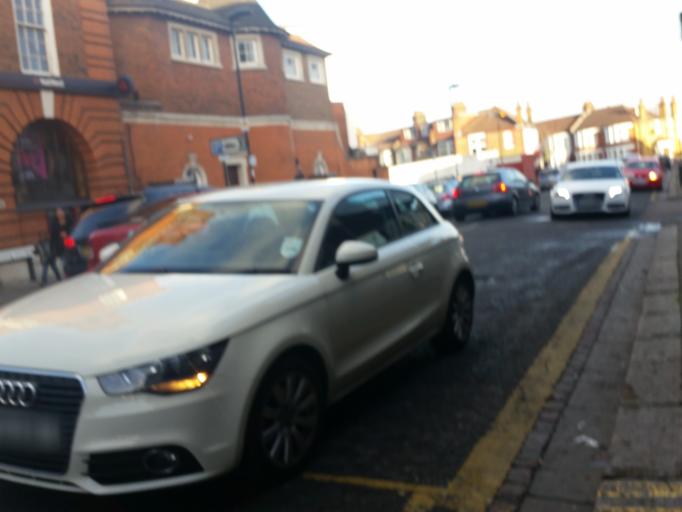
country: GB
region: England
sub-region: Greater London
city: Wood Green
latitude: 51.6182
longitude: -0.1080
